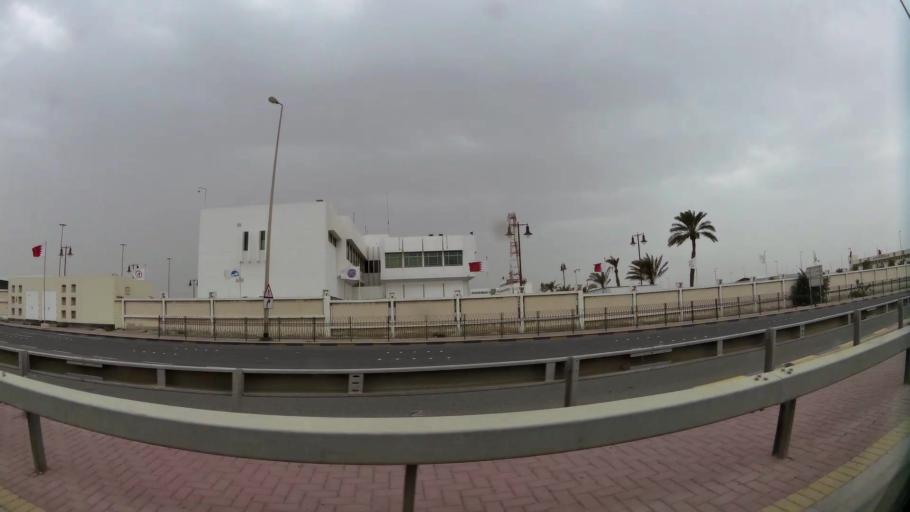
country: BH
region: Northern
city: Madinat `Isa
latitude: 26.1560
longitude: 50.5417
